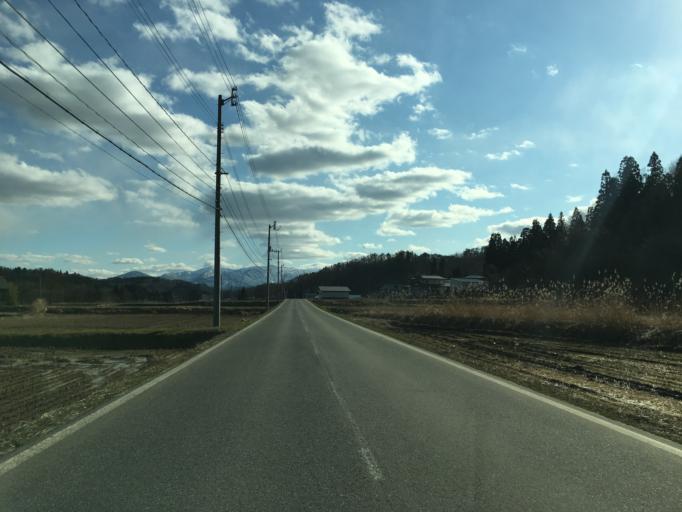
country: JP
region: Yamagata
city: Nagai
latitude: 37.9927
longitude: 140.0058
